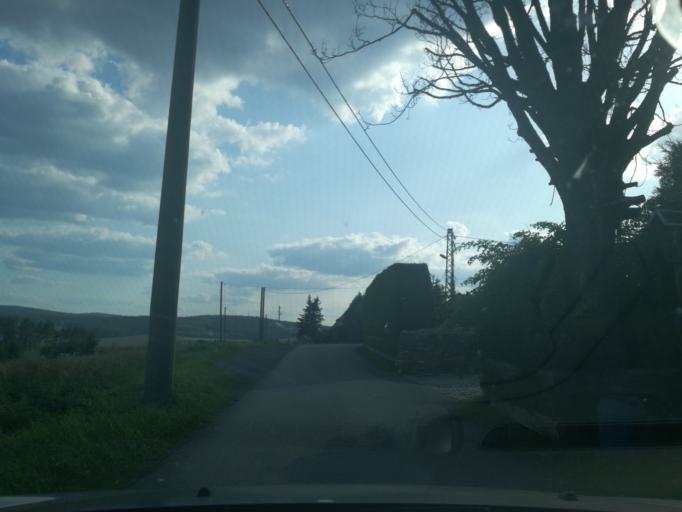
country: DE
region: Saxony
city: Adorf
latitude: 50.3054
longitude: 12.2779
